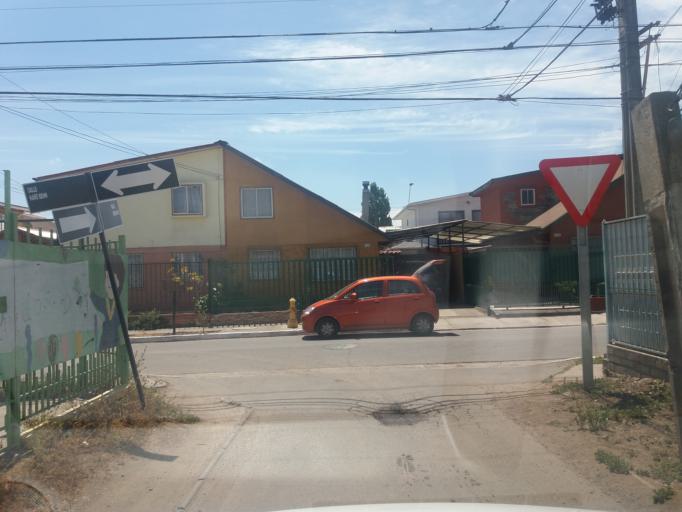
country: CL
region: Valparaiso
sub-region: Provincia de Quillota
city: Hacienda La Calera
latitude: -32.8230
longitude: -71.2250
